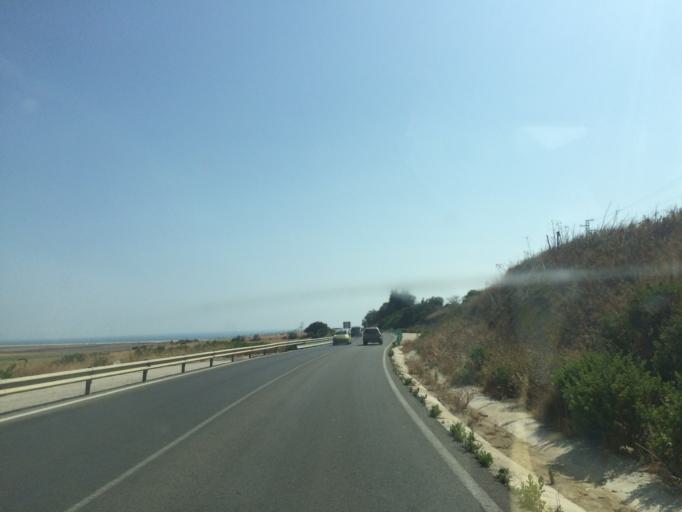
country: ES
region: Andalusia
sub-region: Provincia de Cadiz
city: Conil de la Frontera
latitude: 36.2799
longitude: -6.0750
